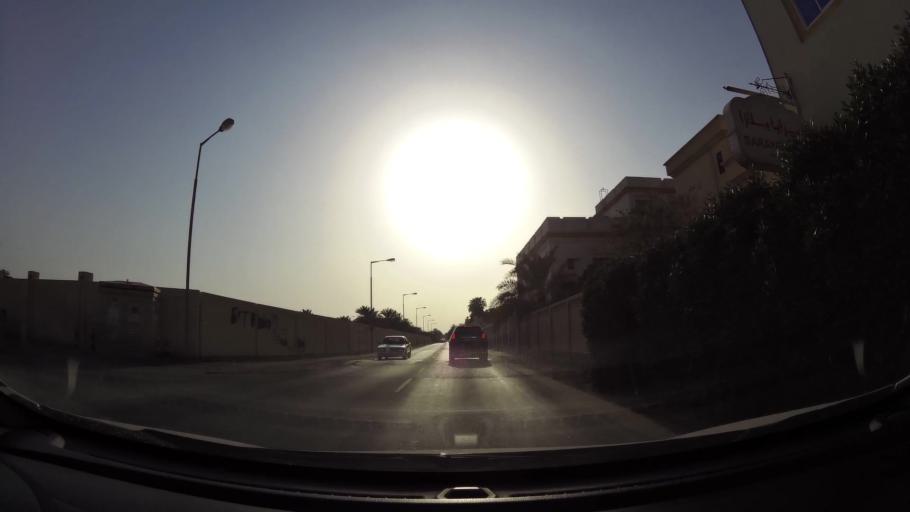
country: BH
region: Manama
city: Jidd Hafs
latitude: 26.2033
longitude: 50.4888
